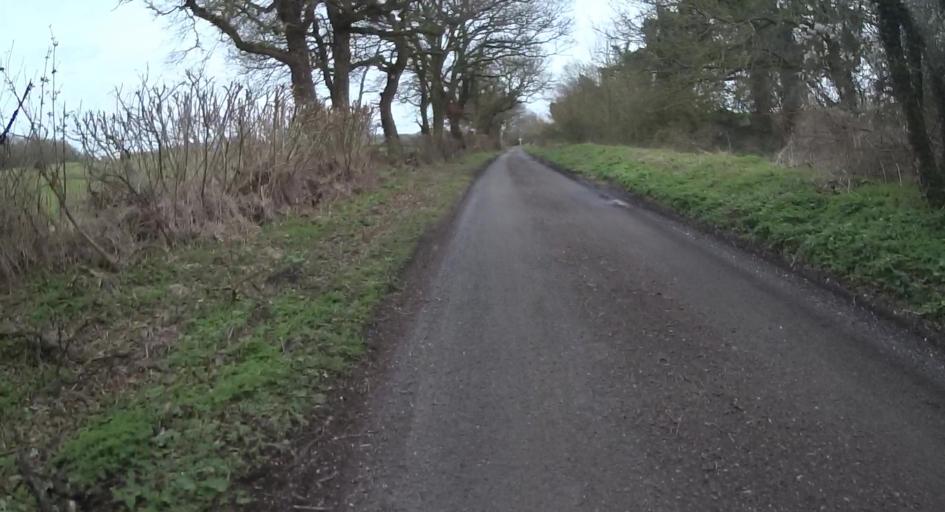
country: GB
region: England
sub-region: Hampshire
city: Overton
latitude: 51.2622
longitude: -1.2428
